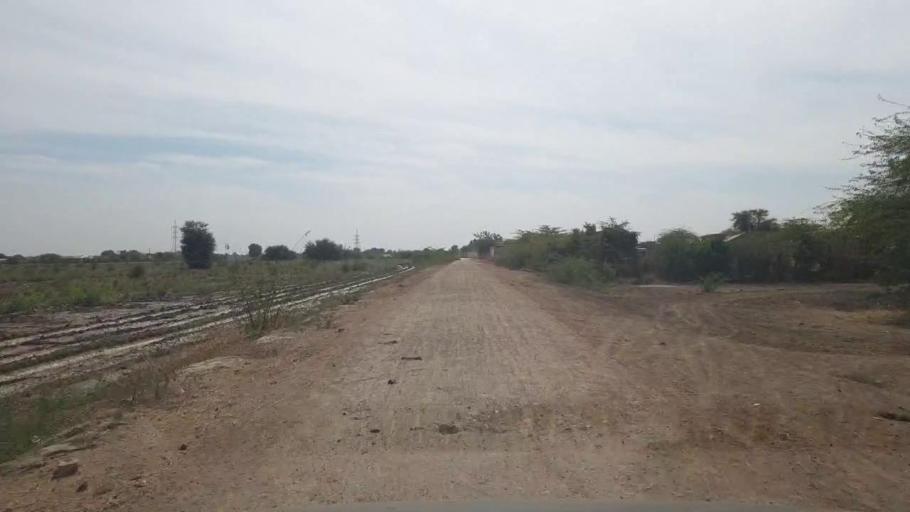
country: PK
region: Sindh
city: Kunri
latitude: 25.3022
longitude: 69.5657
